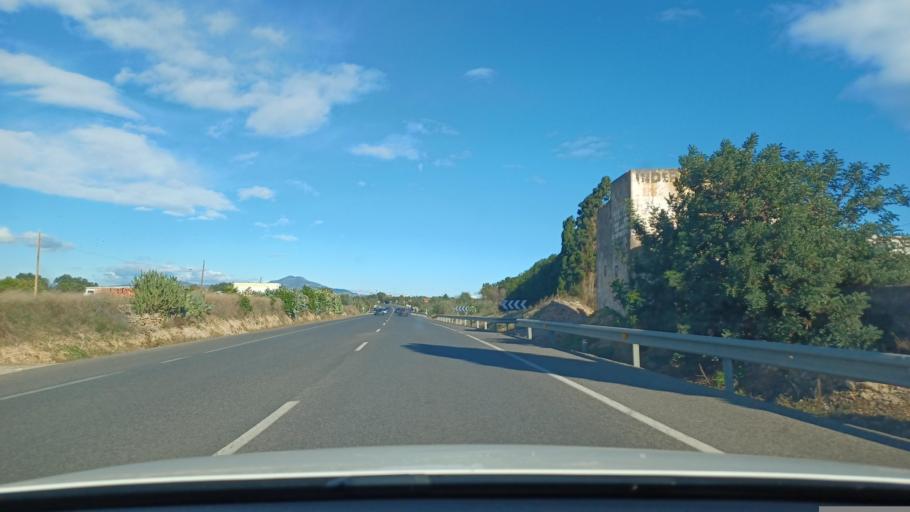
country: ES
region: Valencia
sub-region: Provincia de Castello
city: Benicarlo
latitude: 40.4451
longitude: 0.4471
